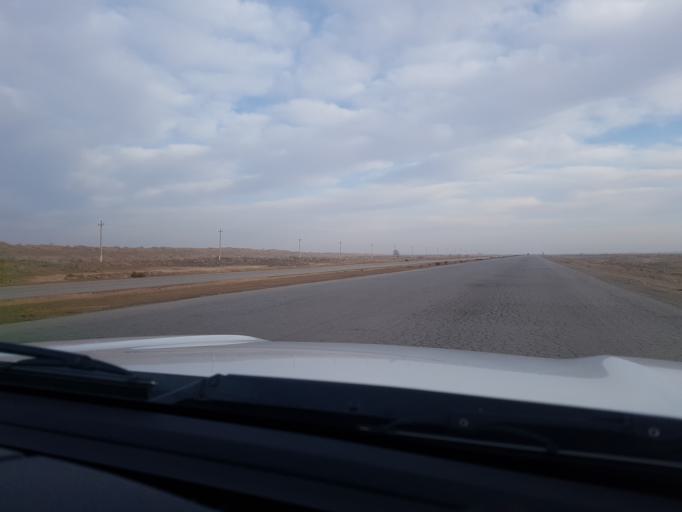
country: TM
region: Ahal
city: Abadan
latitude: 38.6011
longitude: 58.5013
